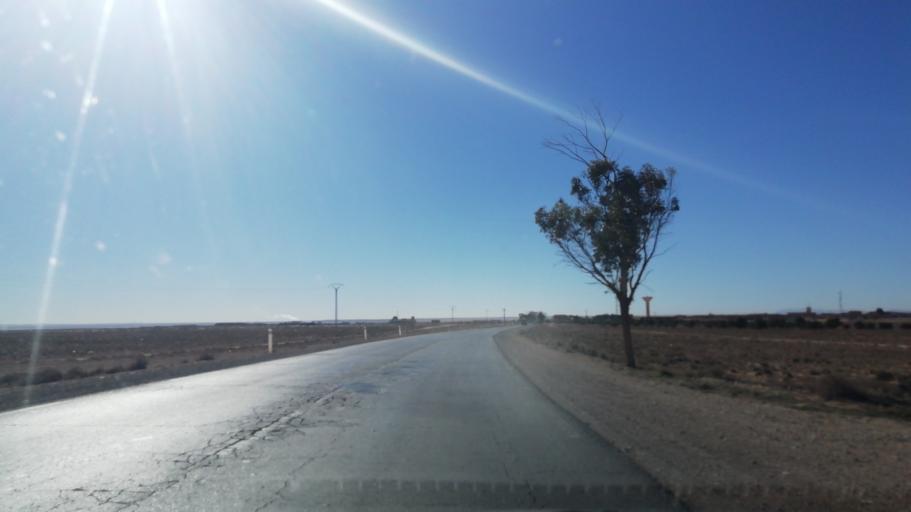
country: DZ
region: Saida
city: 'Ain el Hadjar
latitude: 34.1641
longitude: 0.0720
